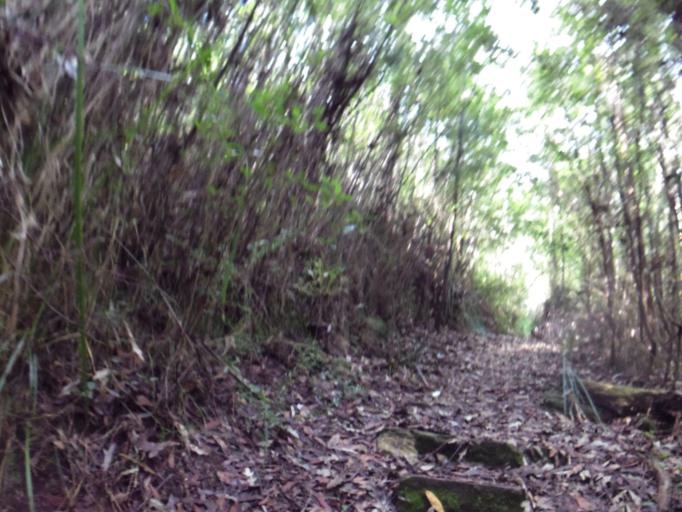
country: AU
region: Victoria
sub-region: Cardinia
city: Bunyip
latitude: -37.9705
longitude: 145.8155
